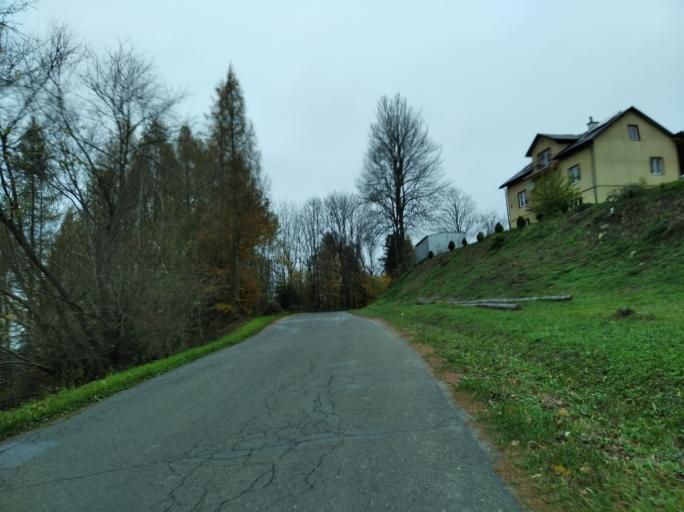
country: PL
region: Subcarpathian Voivodeship
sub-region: Powiat strzyzowski
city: Frysztak
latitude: 49.8358
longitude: 21.6242
